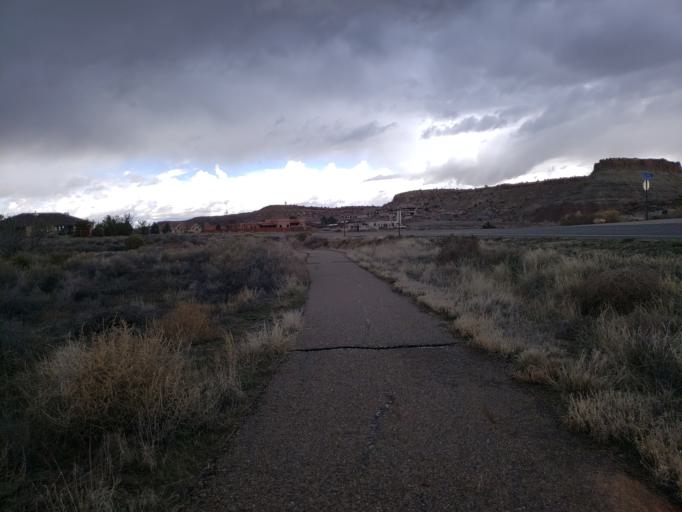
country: US
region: Colorado
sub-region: Mesa County
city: Redlands
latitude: 39.0497
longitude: -108.6356
